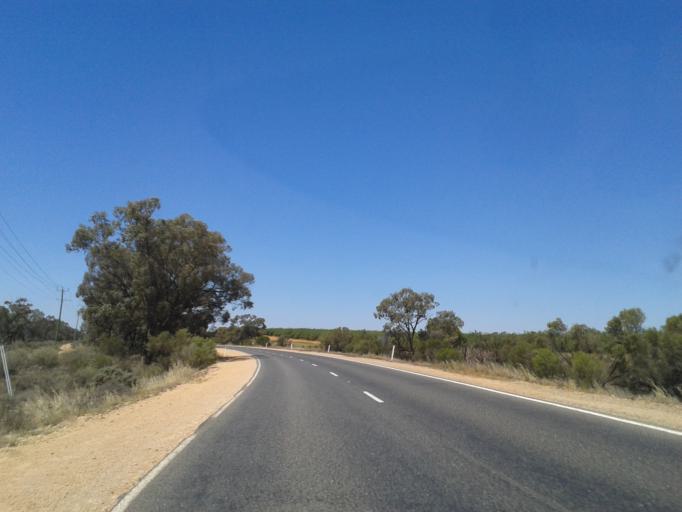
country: AU
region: Victoria
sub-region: Mildura Shire
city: Ouyen
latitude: -34.7184
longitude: 142.9604
